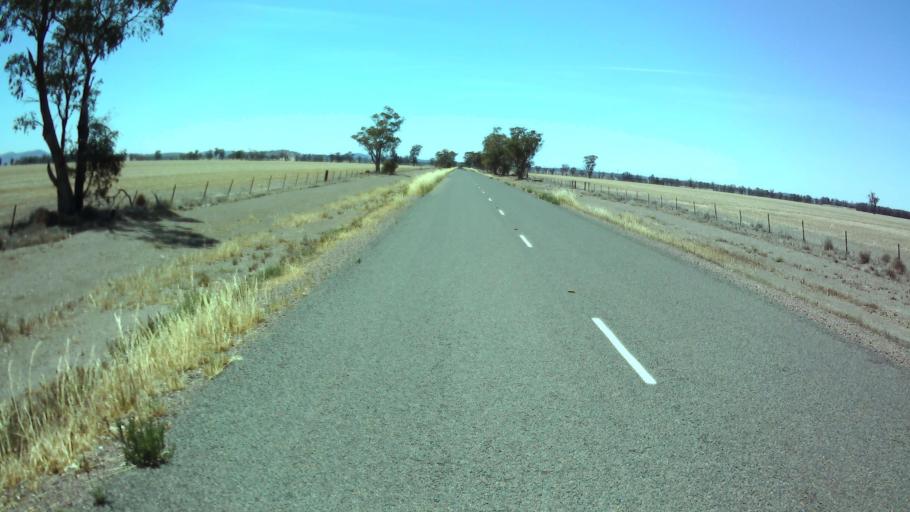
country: AU
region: New South Wales
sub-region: Bland
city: West Wyalong
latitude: -33.6586
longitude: 147.5845
